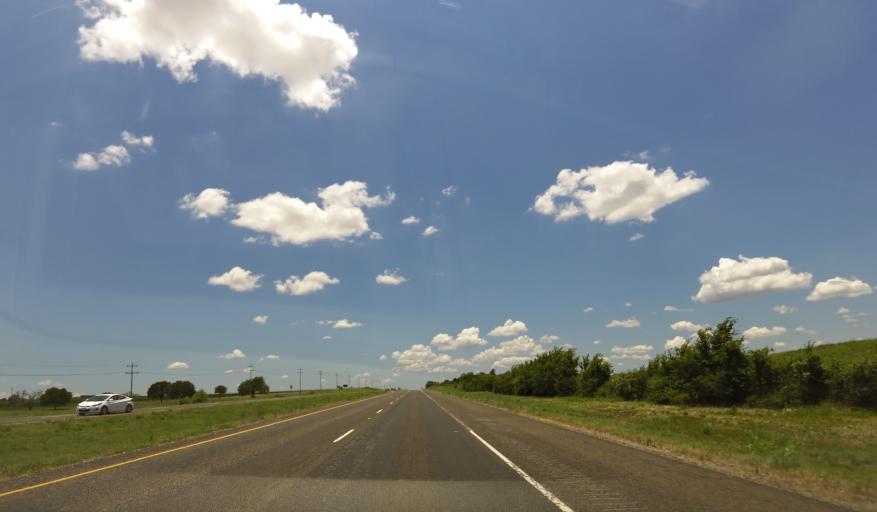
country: US
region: Texas
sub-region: Burleson County
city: Somerville
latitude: 30.1713
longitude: -96.6071
